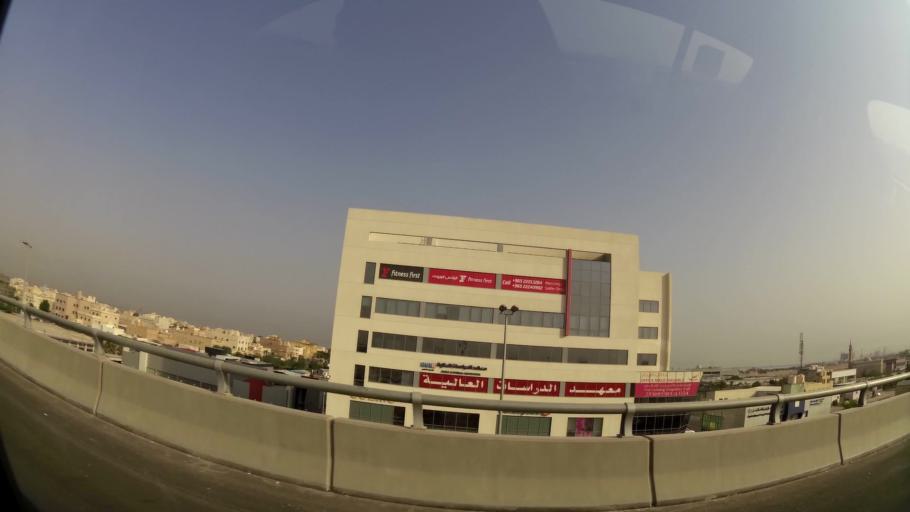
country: KW
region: Al Asimah
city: Ar Rabiyah
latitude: 29.3108
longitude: 47.8630
